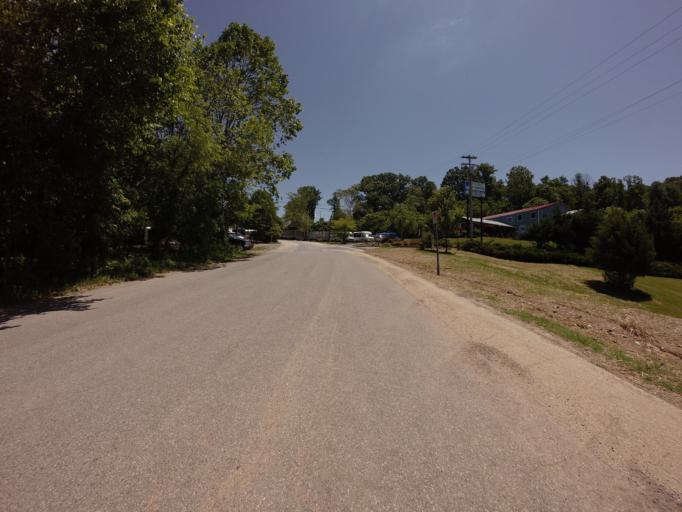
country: US
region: West Virginia
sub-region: Jefferson County
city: Bolivar
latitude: 39.3164
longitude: -77.7696
